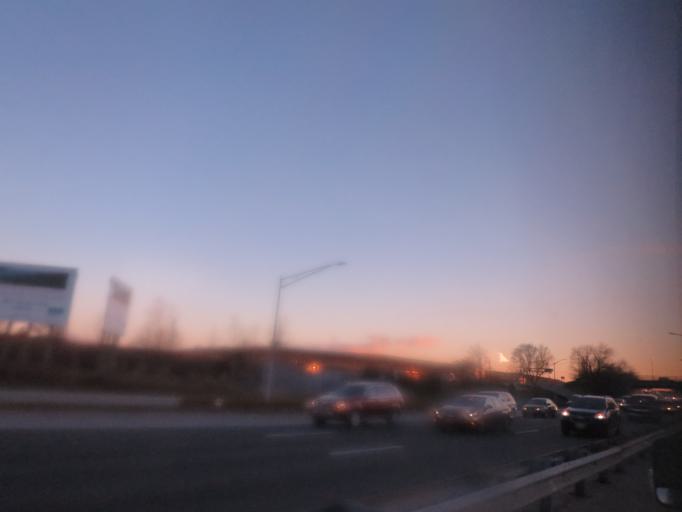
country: US
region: New York
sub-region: Kings County
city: East New York
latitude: 40.6445
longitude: -73.8754
